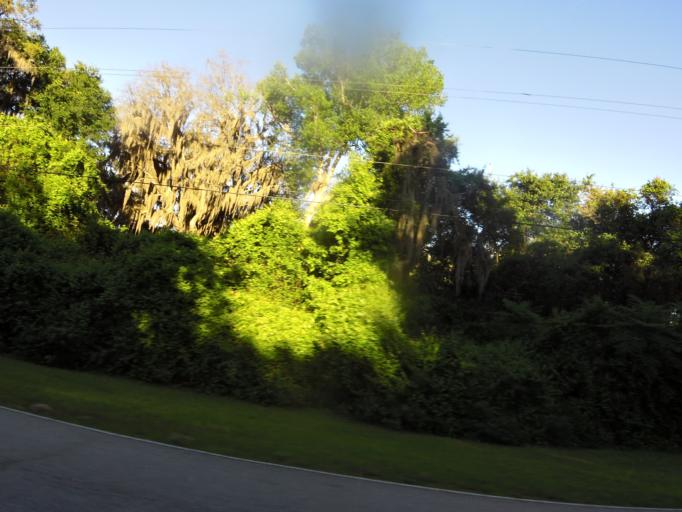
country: US
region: Florida
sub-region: Duval County
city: Atlantic Beach
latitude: 30.3838
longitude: -81.4966
